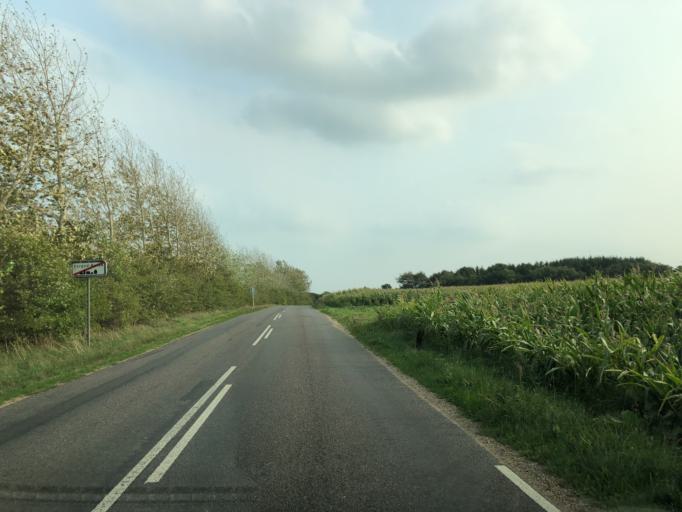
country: DK
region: Central Jutland
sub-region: Ringkobing-Skjern Kommune
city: Videbaek
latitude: 56.0831
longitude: 8.7039
